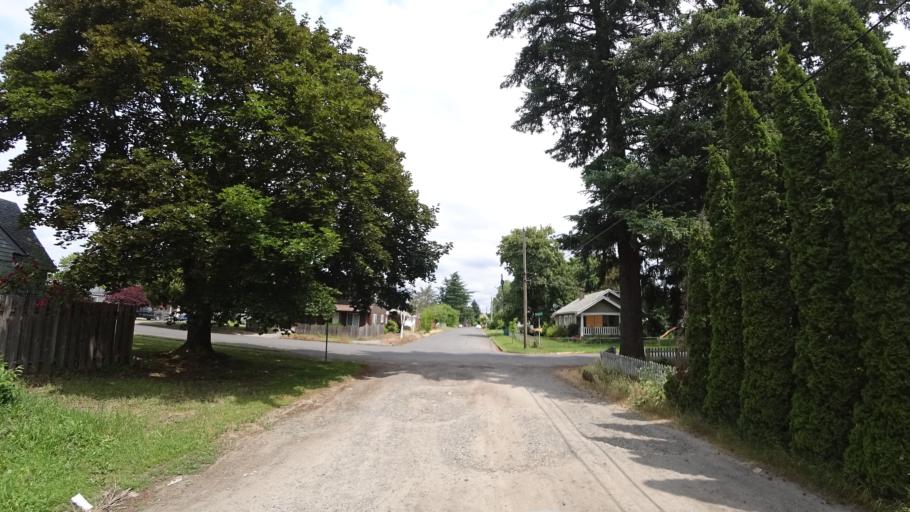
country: US
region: Oregon
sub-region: Multnomah County
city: Lents
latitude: 45.5076
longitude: -122.5726
